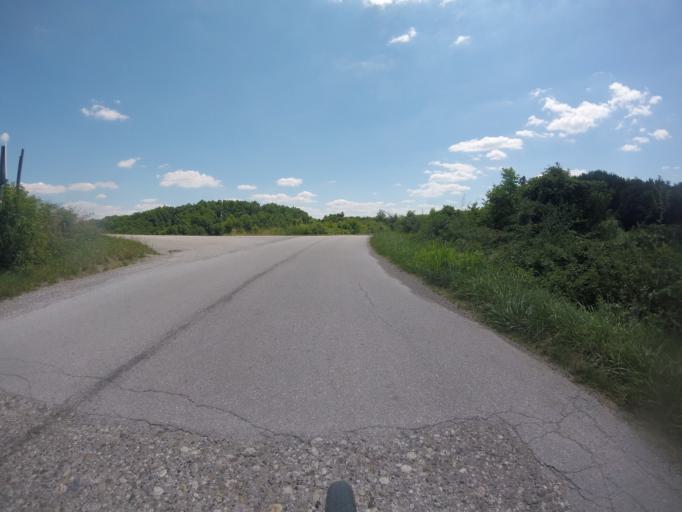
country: HR
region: Karlovacka
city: Ozalj
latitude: 45.6653
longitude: 15.4809
